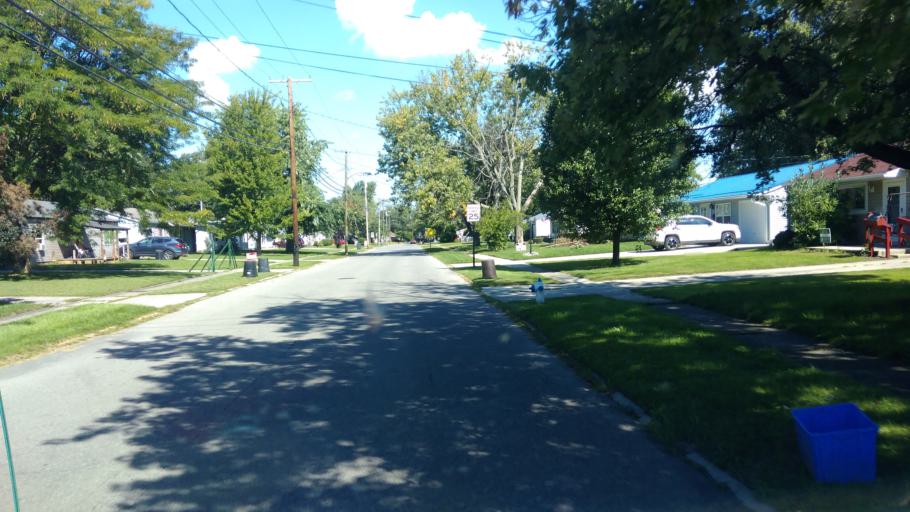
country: US
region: Ohio
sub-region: Marion County
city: Marion
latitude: 40.6056
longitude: -83.1201
